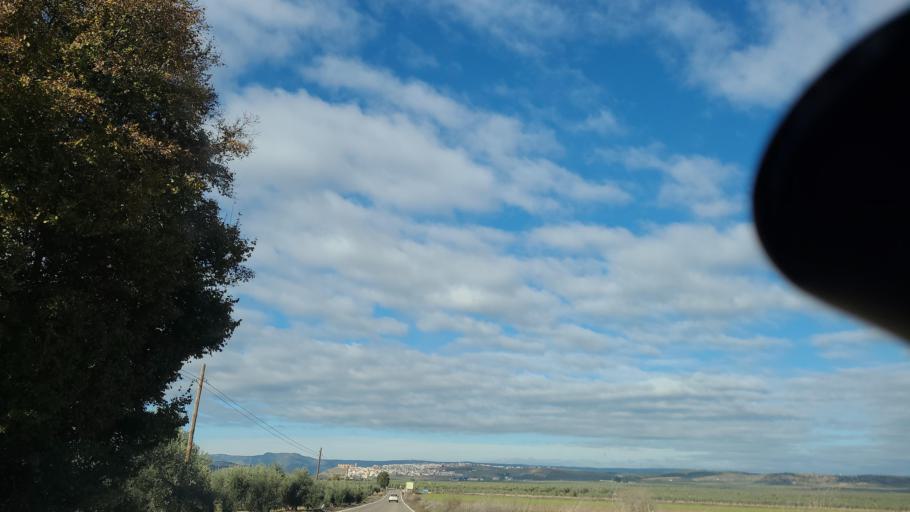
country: ES
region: Andalusia
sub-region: Provincia de Jaen
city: Banos de la Encina
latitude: 38.1492
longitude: -3.7383
